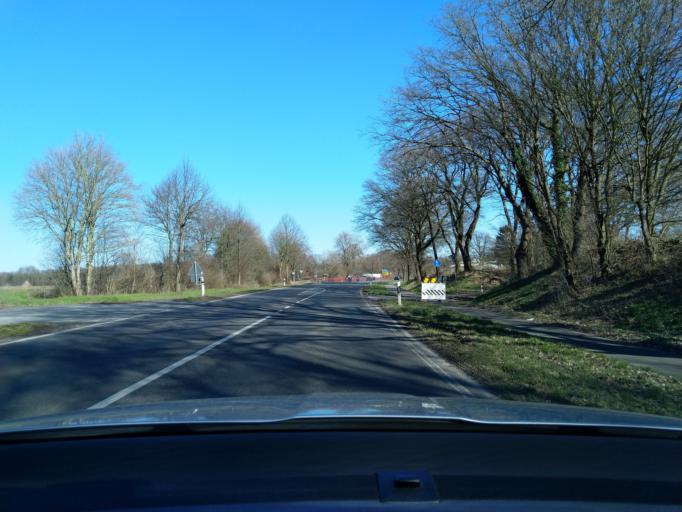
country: DE
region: North Rhine-Westphalia
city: Wegberg
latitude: 51.1487
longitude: 6.2698
